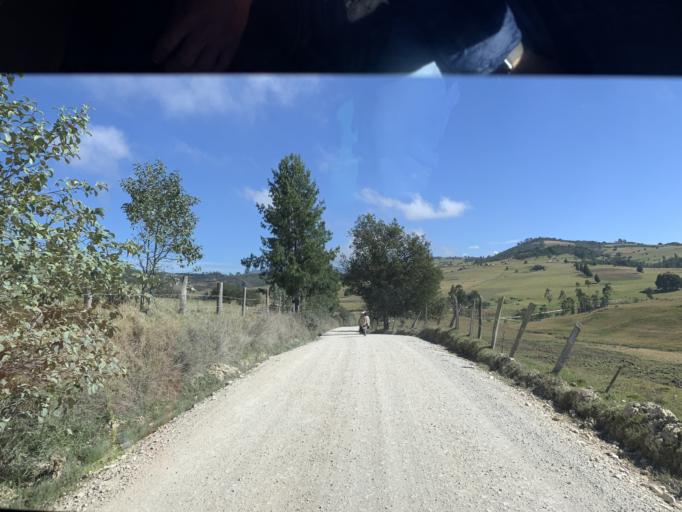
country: CO
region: Boyaca
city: Tuta
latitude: 5.6769
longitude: -73.1465
